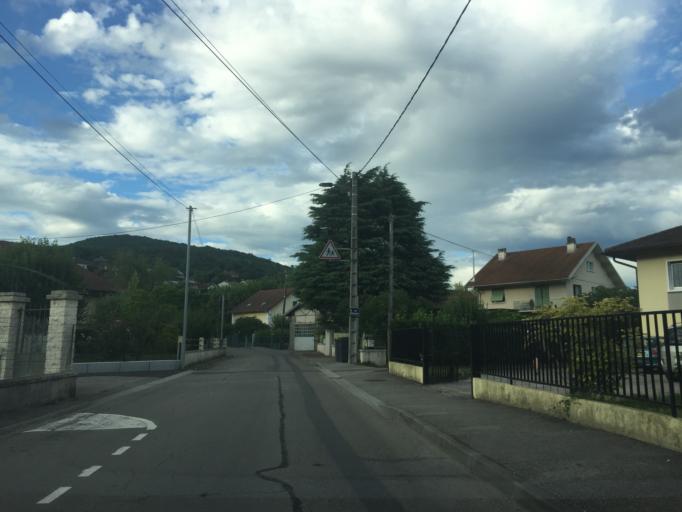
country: FR
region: Rhone-Alpes
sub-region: Departement de la Savoie
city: Brison-Saint-Innocent
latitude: 45.7032
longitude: 5.9005
